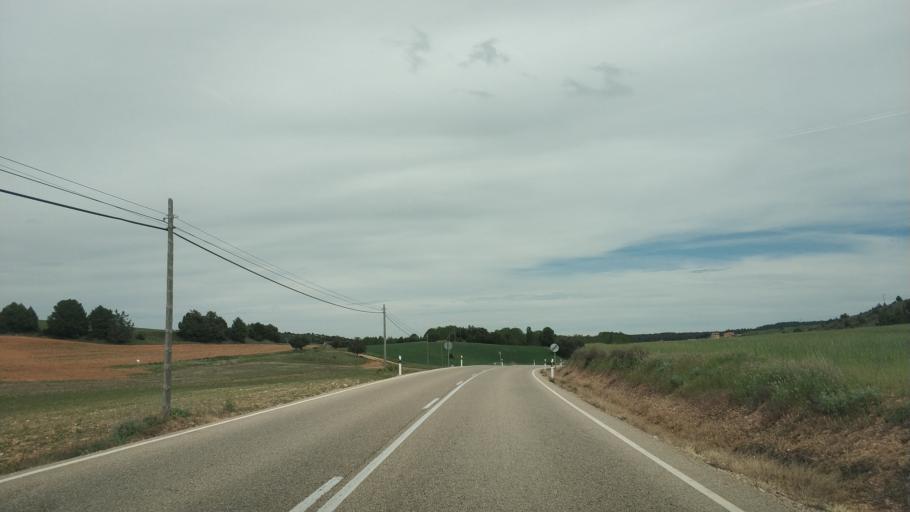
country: ES
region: Castille and Leon
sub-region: Provincia de Soria
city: El Burgo de Osma
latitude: 41.5746
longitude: -3.0205
